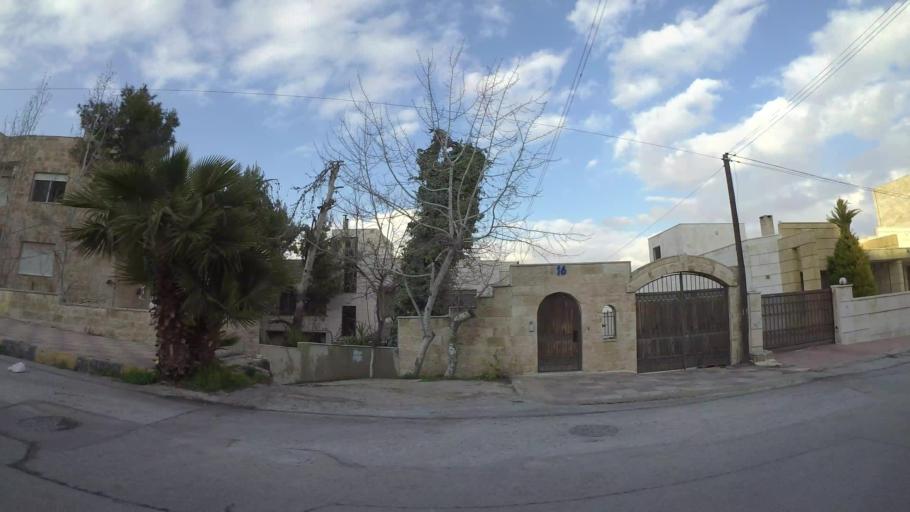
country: JO
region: Amman
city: Al Jubayhah
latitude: 31.9760
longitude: 35.8830
